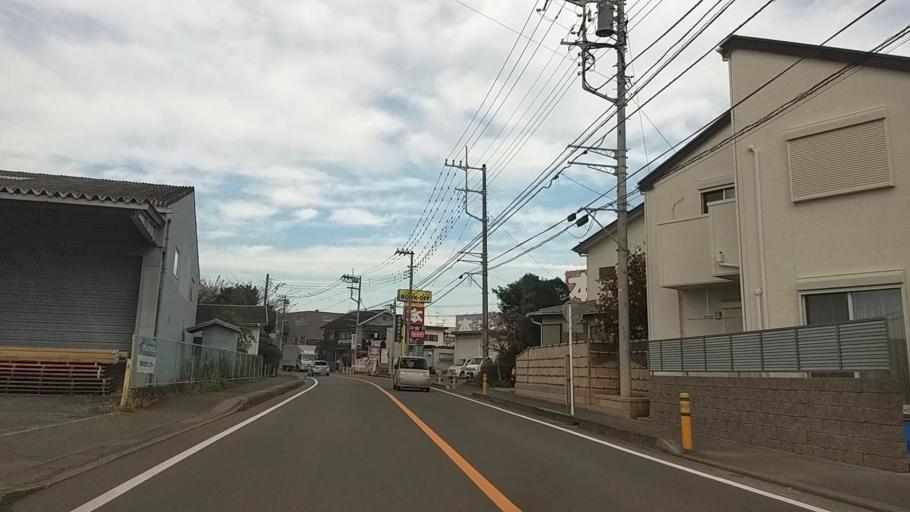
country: JP
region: Kanagawa
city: Atsugi
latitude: 35.4019
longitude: 139.4232
